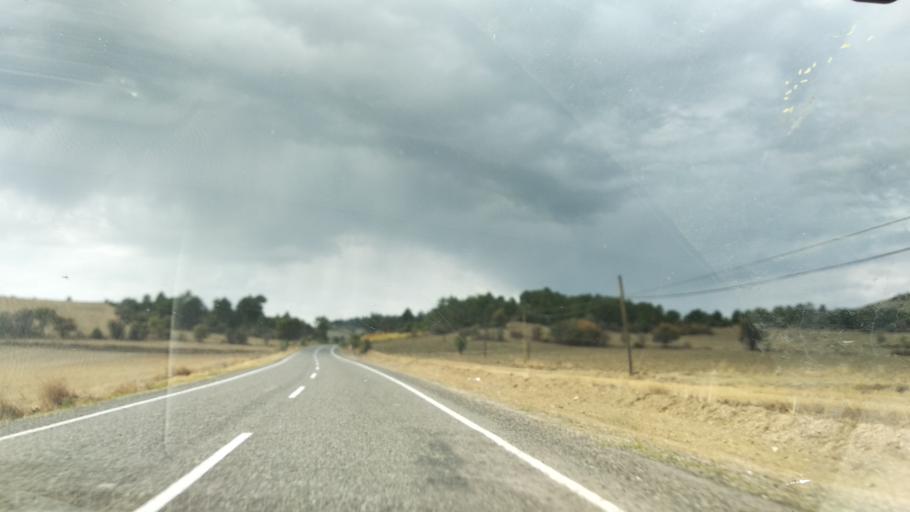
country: TR
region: Bolu
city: Seben
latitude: 40.3610
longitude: 31.4920
